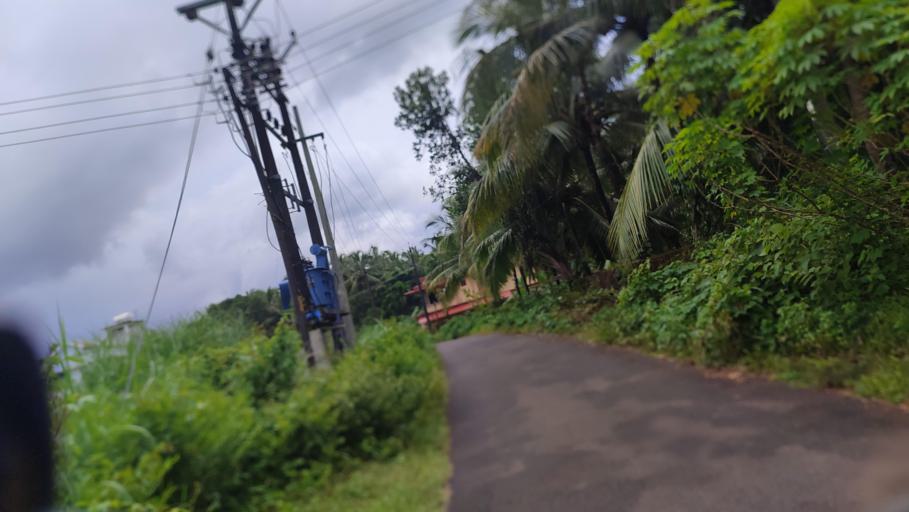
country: IN
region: Kerala
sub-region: Kasaragod District
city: Kannangad
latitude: 12.4011
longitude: 75.0572
